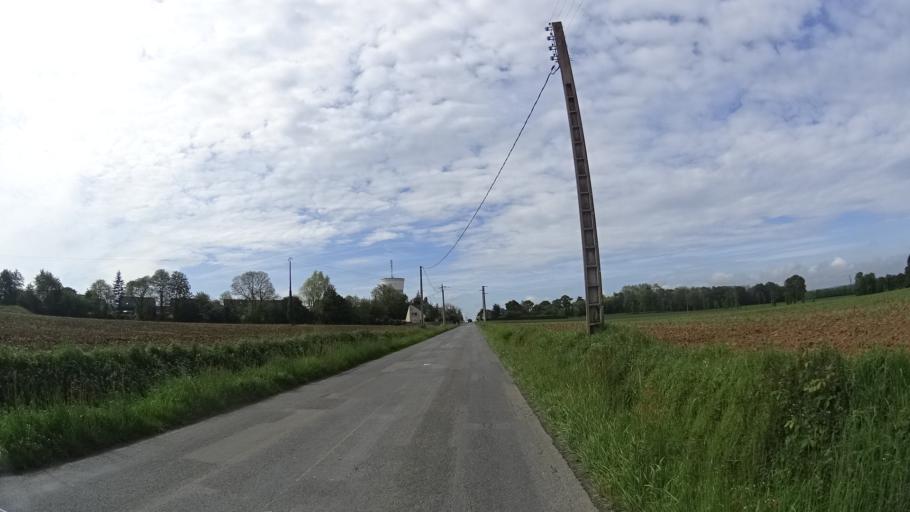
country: FR
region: Brittany
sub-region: Departement d'Ille-et-Vilaine
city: Mordelles
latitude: 48.0824
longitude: -1.8429
